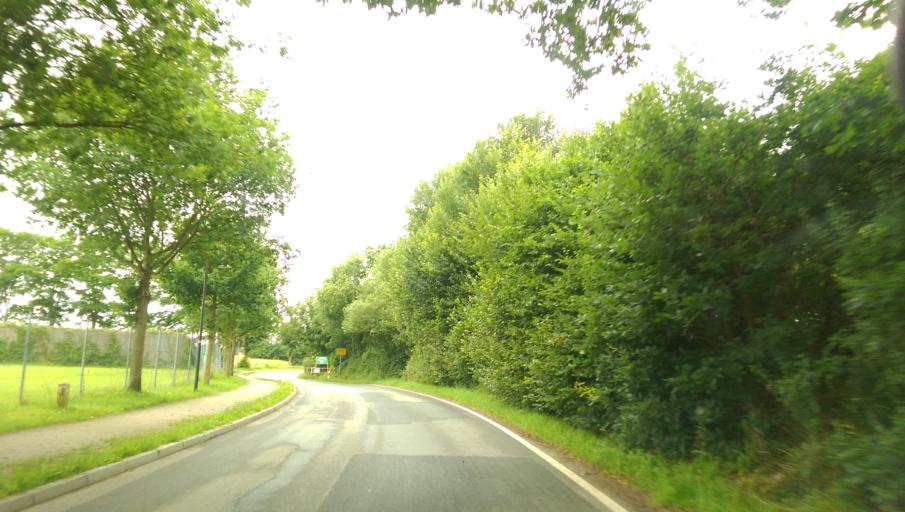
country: DE
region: Schleswig-Holstein
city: Ratekau
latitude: 53.9887
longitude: 10.6736
